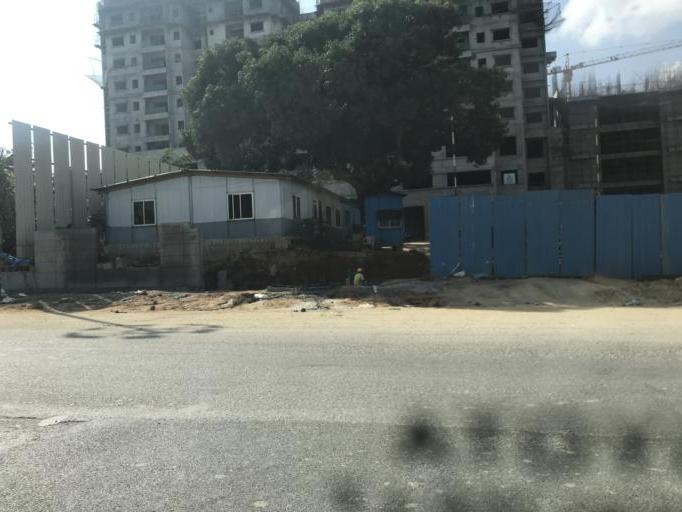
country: IN
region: Karnataka
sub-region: Bangalore Urban
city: Bangalore
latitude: 12.8453
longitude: 77.5882
